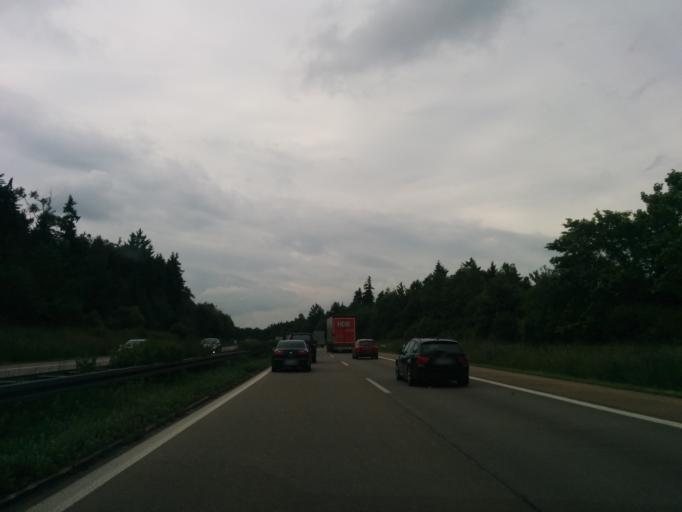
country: DE
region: Baden-Wuerttemberg
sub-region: Regierungsbezirk Stuttgart
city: Ellenberg
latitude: 49.0800
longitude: 10.2042
